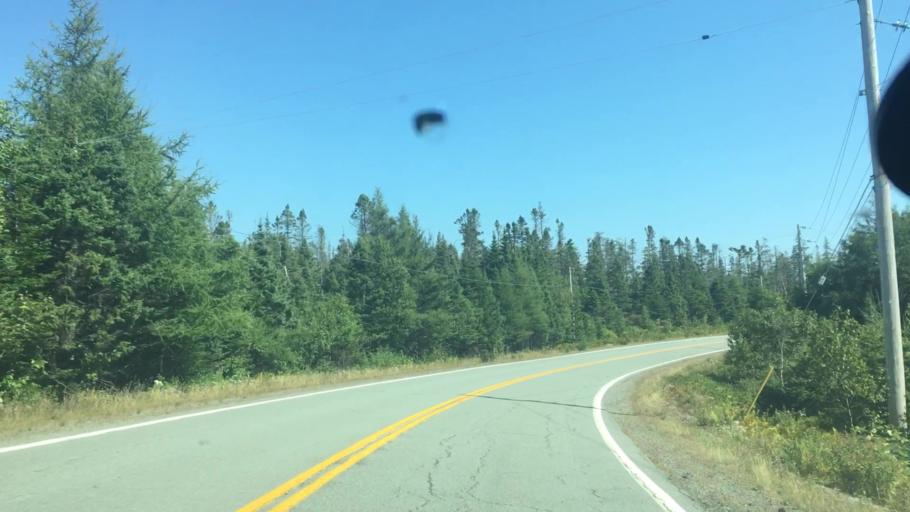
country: CA
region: Nova Scotia
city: Antigonish
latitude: 45.0132
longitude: -62.1045
